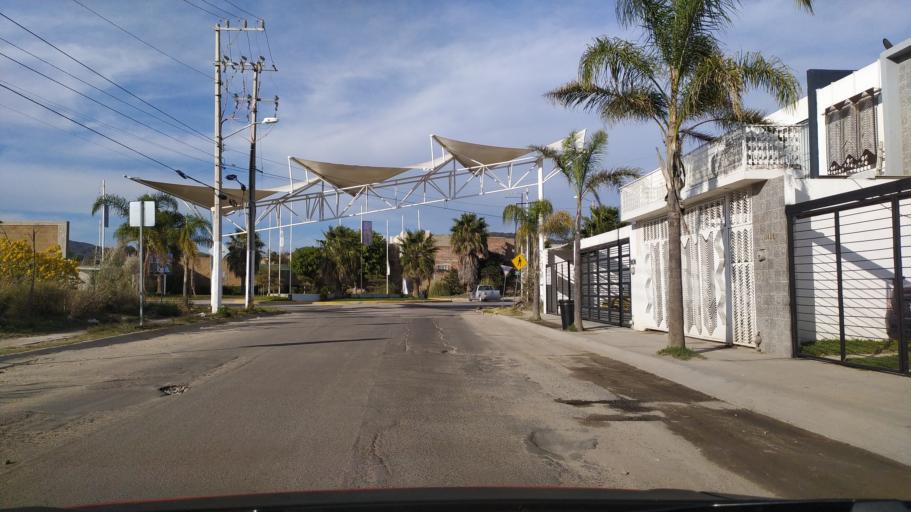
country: MX
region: Jalisco
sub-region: Tlajomulco de Zuniga
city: Palomar
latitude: 20.6307
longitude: -103.4770
